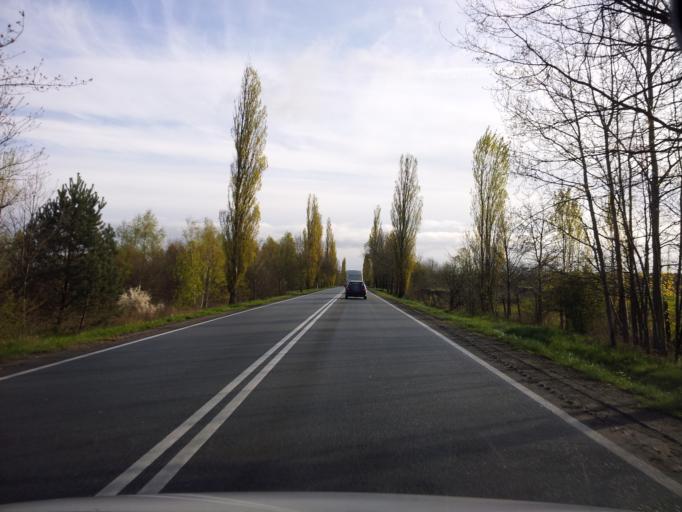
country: PL
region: Lubusz
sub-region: Powiat zielonogorski
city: Nowogrod Bobrzanski
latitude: 51.8035
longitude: 15.2567
